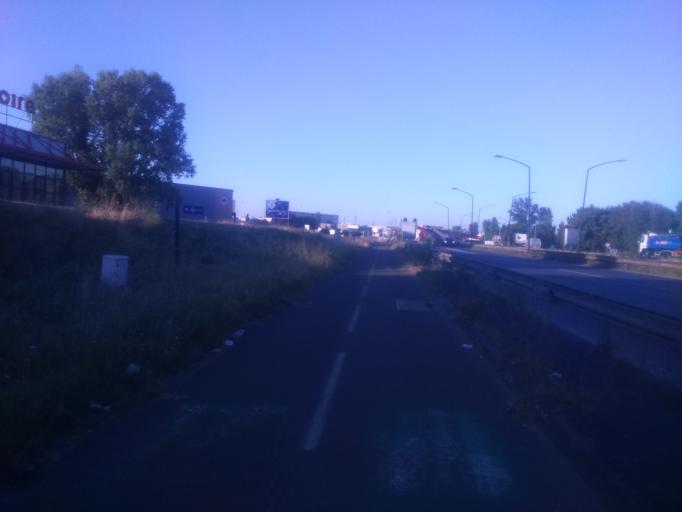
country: FR
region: Aquitaine
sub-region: Departement de la Gironde
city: Le Bouscat
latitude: 44.8722
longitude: -0.5656
